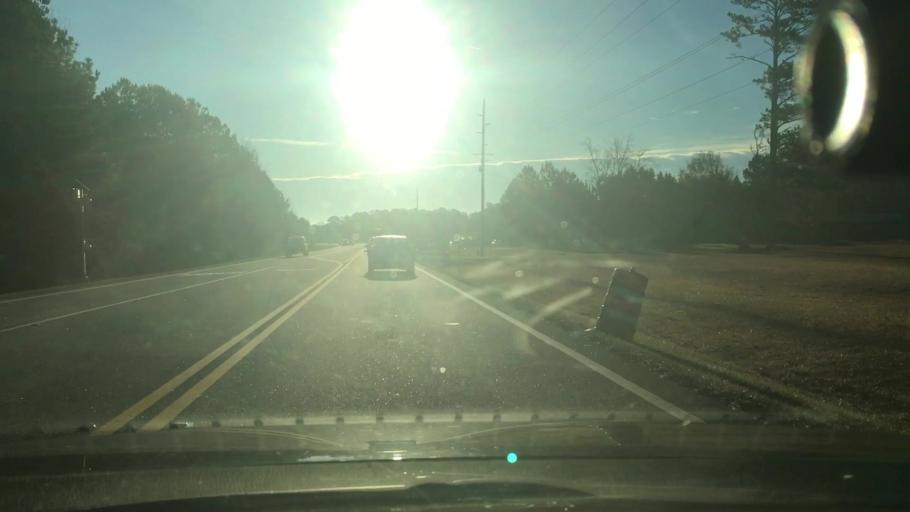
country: US
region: Georgia
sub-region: Coweta County
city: Senoia
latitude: 33.2958
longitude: -84.5857
